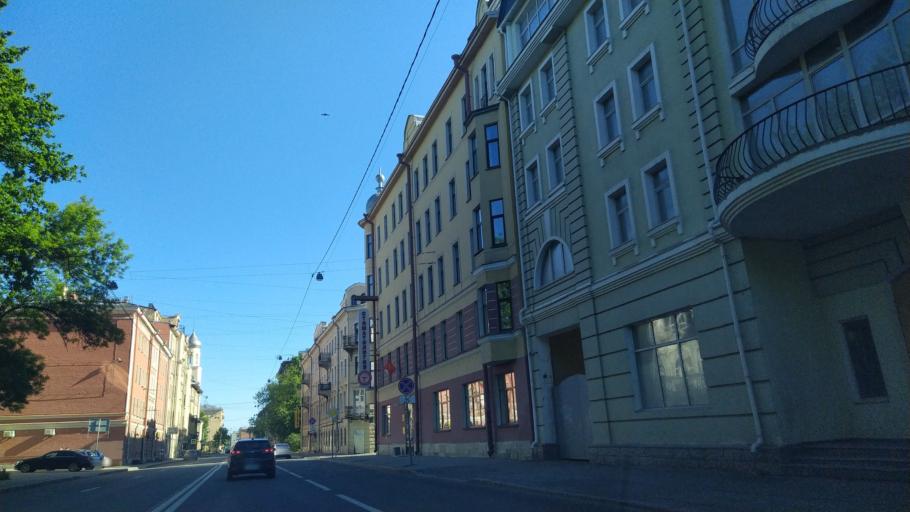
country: RU
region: Leningrad
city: Sampsonievskiy
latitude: 59.9736
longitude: 30.3396
